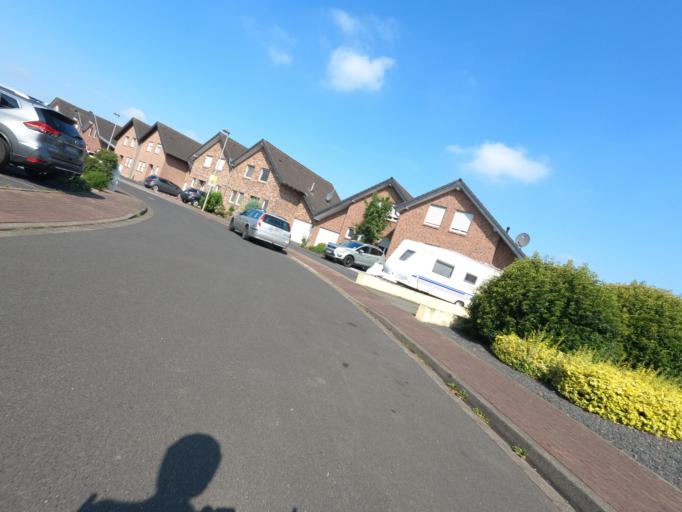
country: DE
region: North Rhine-Westphalia
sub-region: Regierungsbezirk Koln
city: Heinsberg
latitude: 51.0731
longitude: 6.1040
